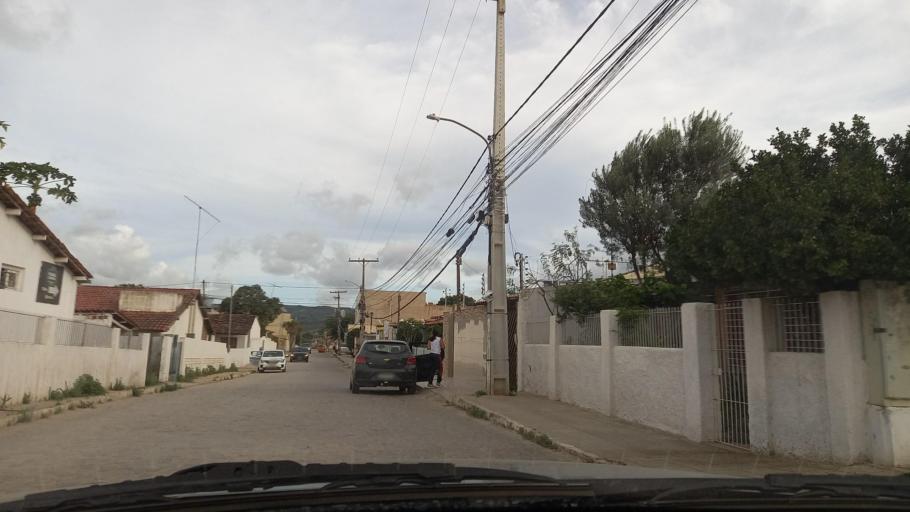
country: BR
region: Pernambuco
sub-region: Gravata
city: Gravata
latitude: -8.1987
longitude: -35.5593
